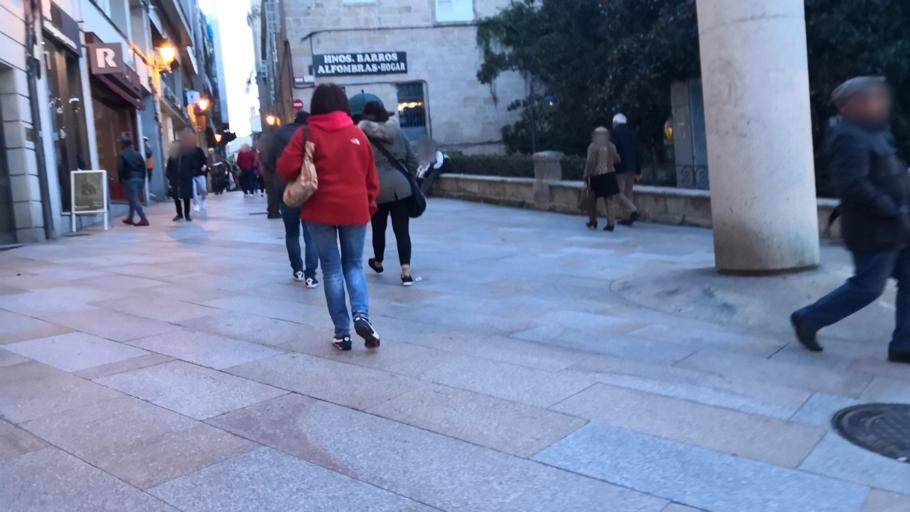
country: ES
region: Galicia
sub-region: Provincia de Ourense
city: Ourense
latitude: 42.3378
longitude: -7.8645
